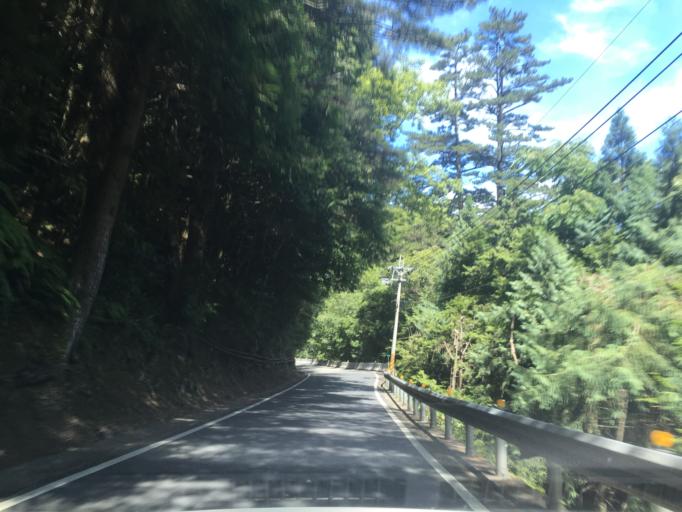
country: TW
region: Taiwan
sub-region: Nantou
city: Puli
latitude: 24.2216
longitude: 121.2621
